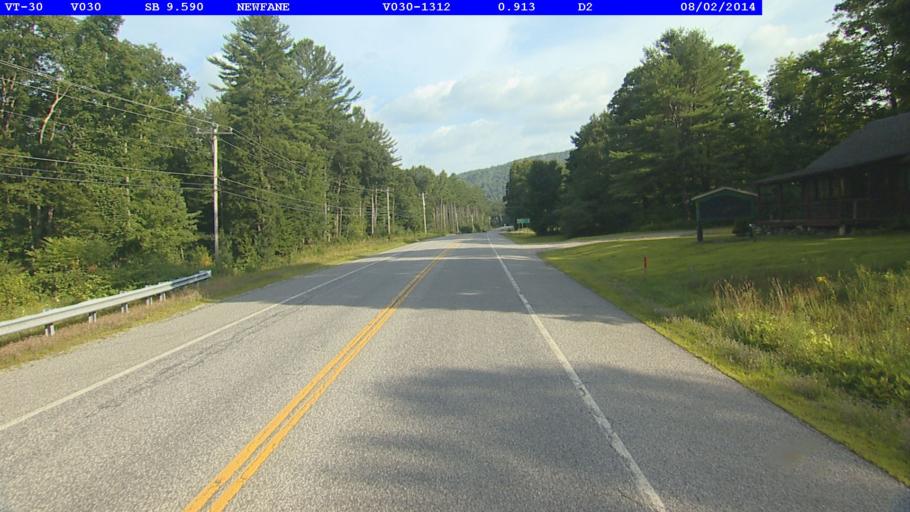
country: US
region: Vermont
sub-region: Windham County
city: Newfane
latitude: 42.9586
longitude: -72.6505
